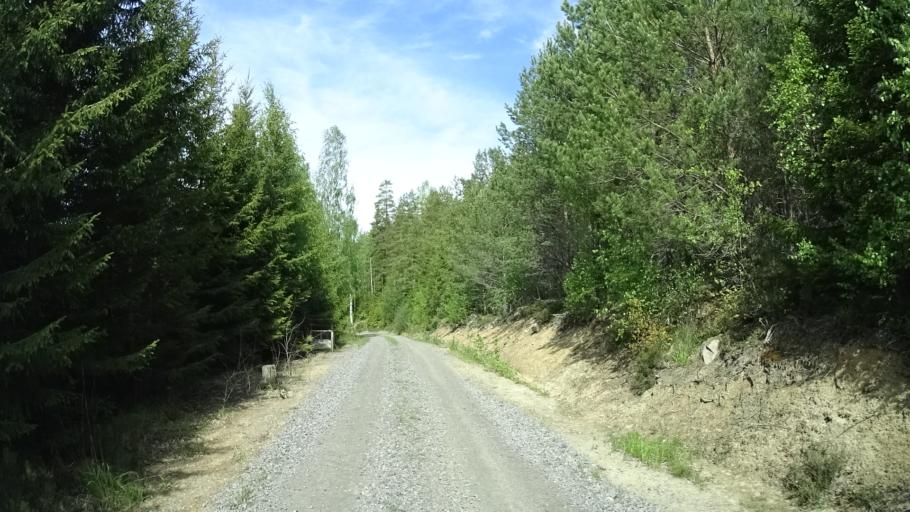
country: SE
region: OEstergoetland
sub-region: Finspangs Kommun
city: Finspang
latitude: 58.7961
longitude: 15.8522
